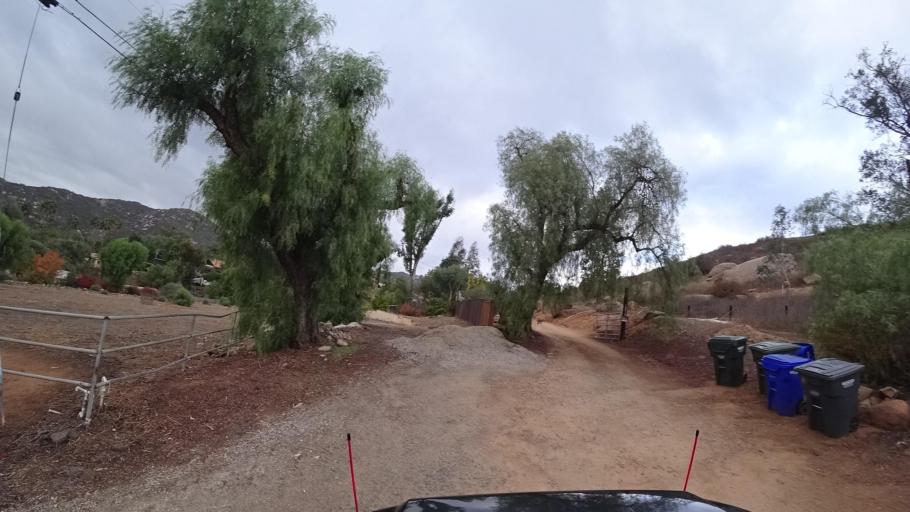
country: US
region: California
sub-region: San Diego County
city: Eucalyptus Hills
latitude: 32.8736
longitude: -116.9431
